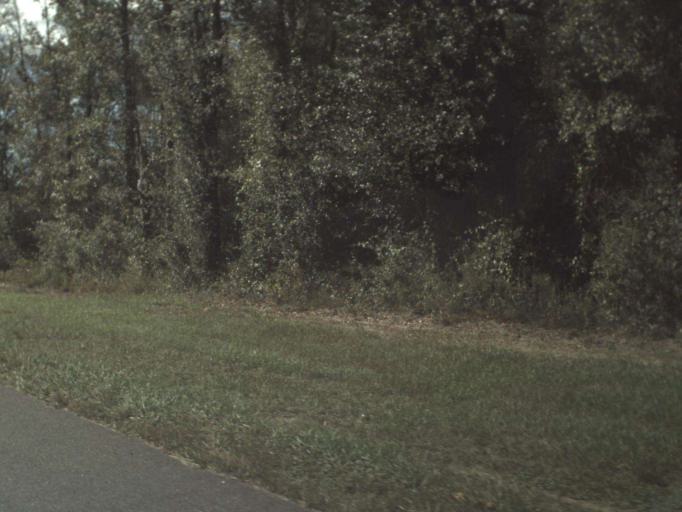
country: US
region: Florida
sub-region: Holmes County
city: Bonifay
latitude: 30.6861
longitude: -85.6321
